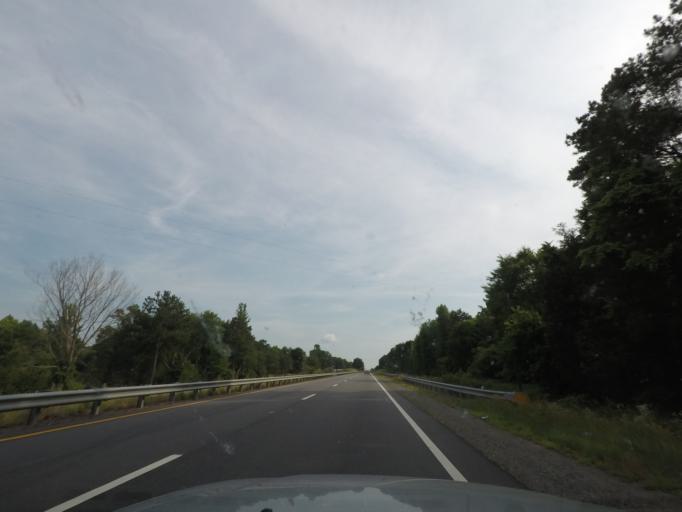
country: US
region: Virginia
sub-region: Mecklenburg County
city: Chase City
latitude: 36.9454
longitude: -78.5019
